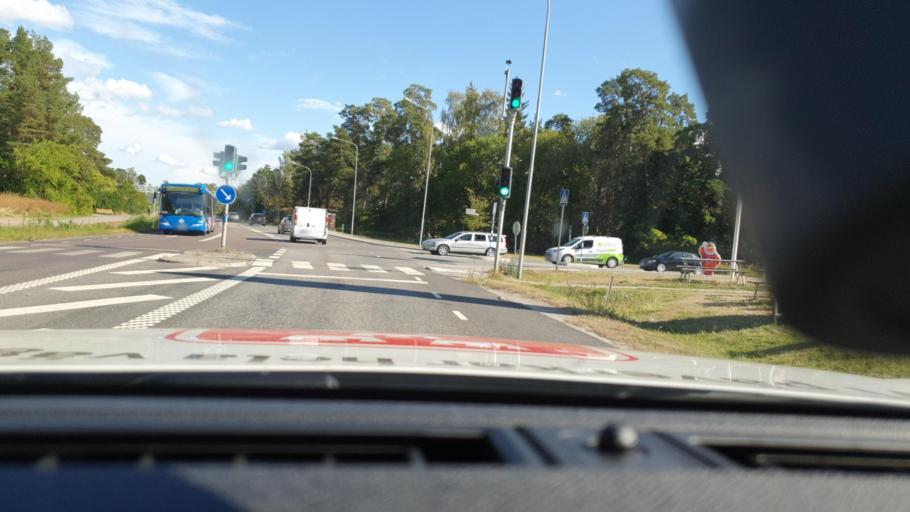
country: SE
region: Stockholm
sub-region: Vaxholms Kommun
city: Resaro
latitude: 59.4035
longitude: 18.3254
